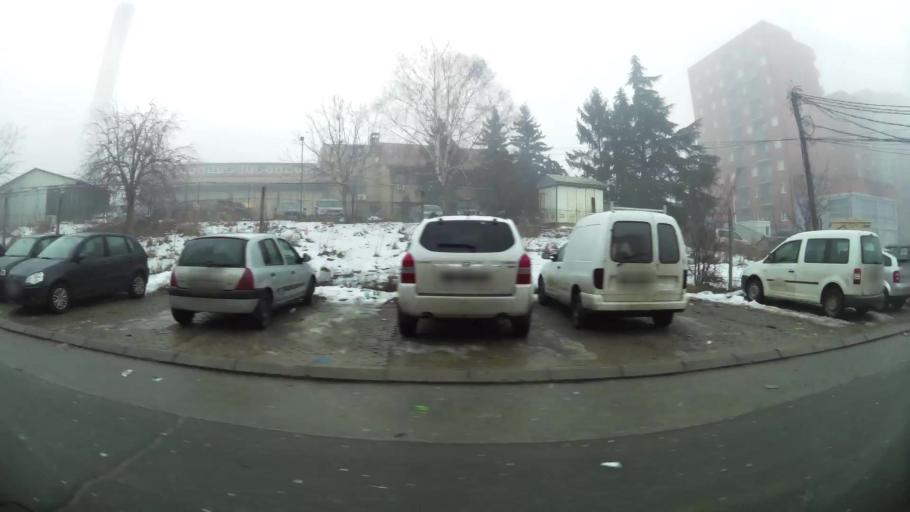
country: XK
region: Pristina
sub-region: Komuna e Prishtines
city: Pristina
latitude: 42.6473
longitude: 21.1533
